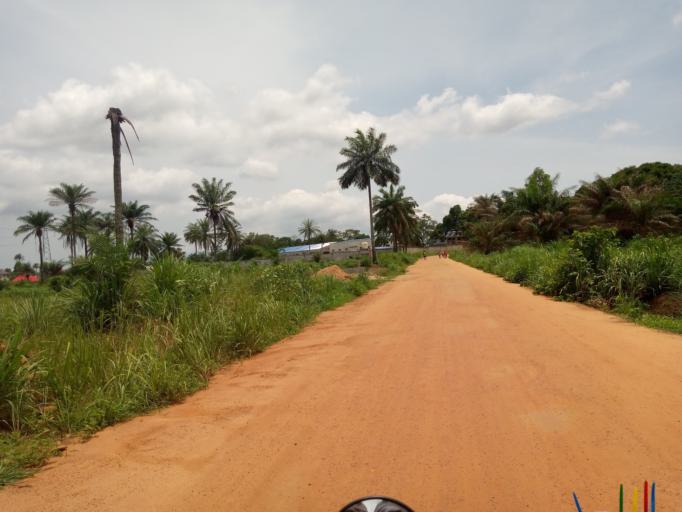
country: SL
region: Western Area
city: Waterloo
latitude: 8.3579
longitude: -12.9687
